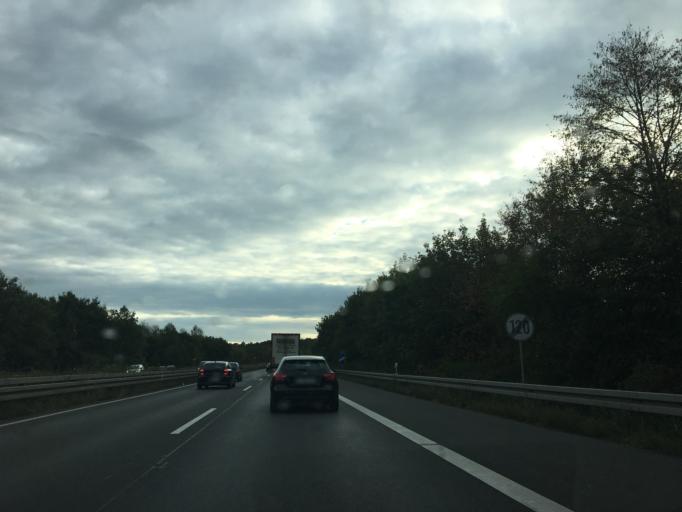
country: DE
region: Hesse
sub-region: Regierungsbezirk Giessen
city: Giessen
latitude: 50.5701
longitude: 8.7027
